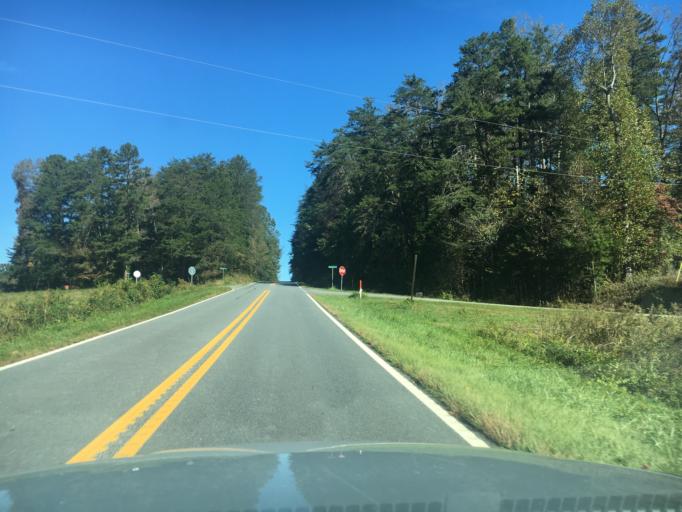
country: US
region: North Carolina
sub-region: Rutherford County
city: Spindale
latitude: 35.4618
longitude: -81.8856
